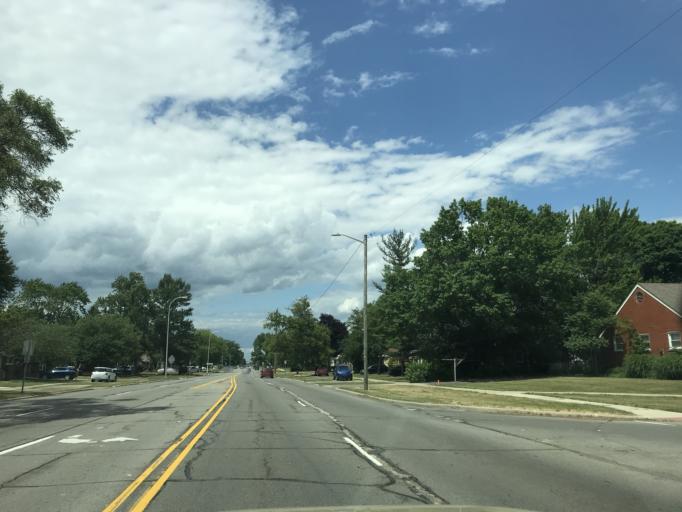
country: US
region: Michigan
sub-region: Wayne County
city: Redford
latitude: 42.3628
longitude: -83.3131
